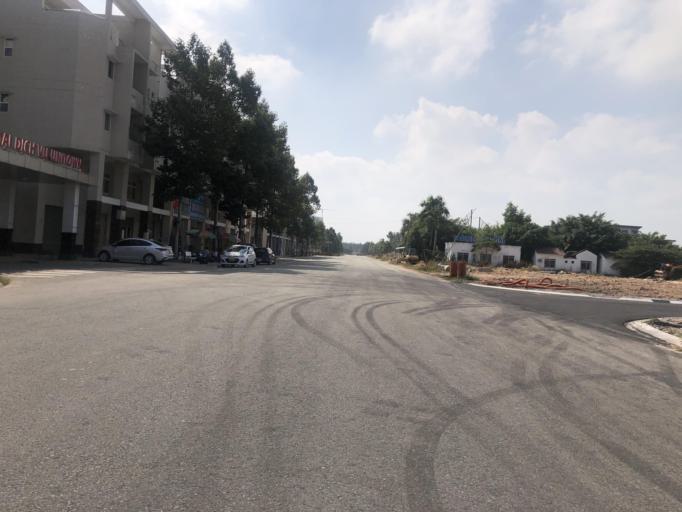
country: VN
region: Binh Duong
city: Thu Dau Mot
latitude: 11.0717
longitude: 106.6830
